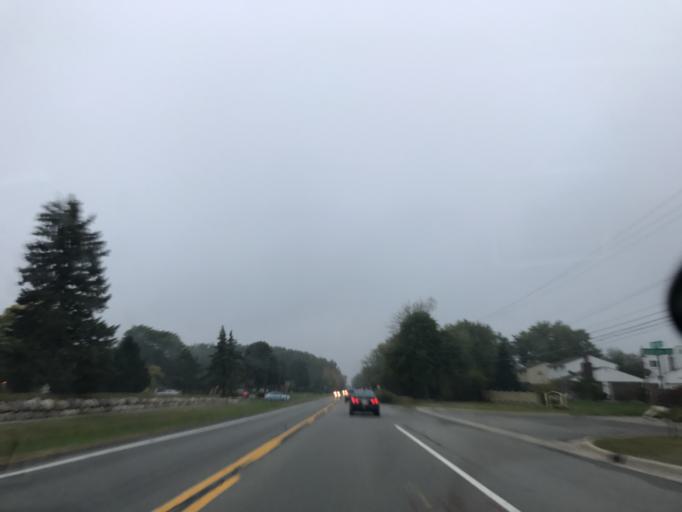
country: US
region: Michigan
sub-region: Oakland County
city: Franklin
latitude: 42.4826
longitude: -83.3188
